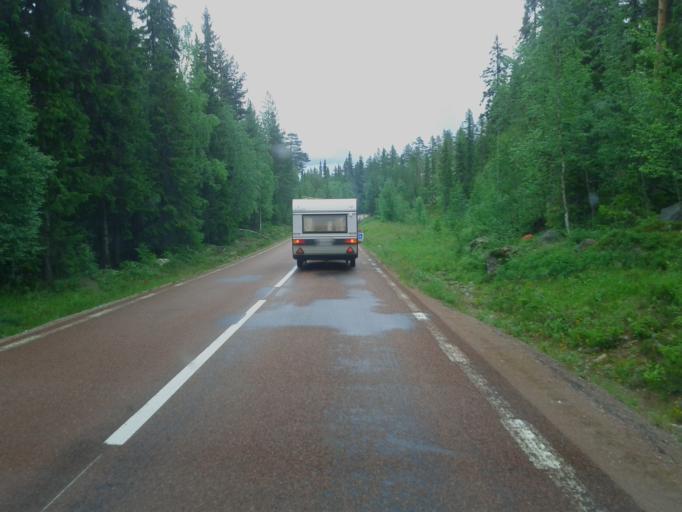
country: NO
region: Hedmark
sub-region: Trysil
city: Innbygda
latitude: 61.8518
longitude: 12.6522
